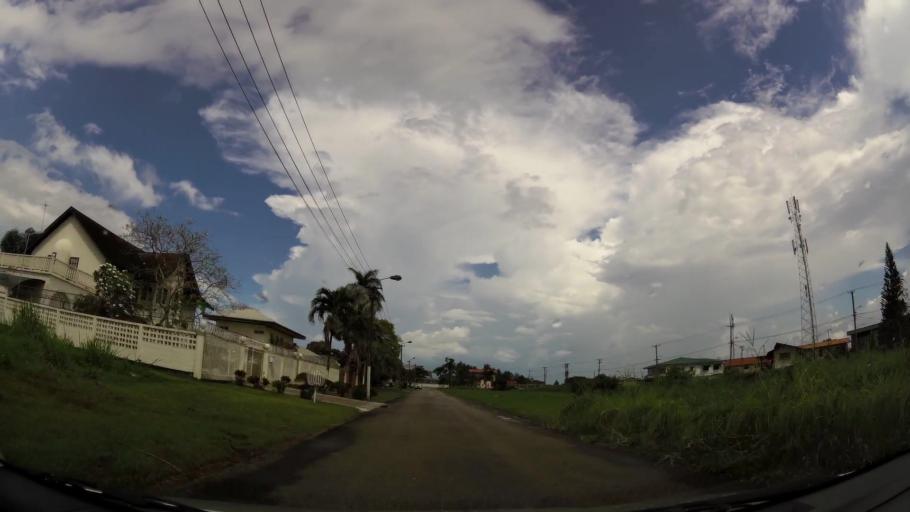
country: SR
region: Paramaribo
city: Paramaribo
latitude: 5.8361
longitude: -55.1320
